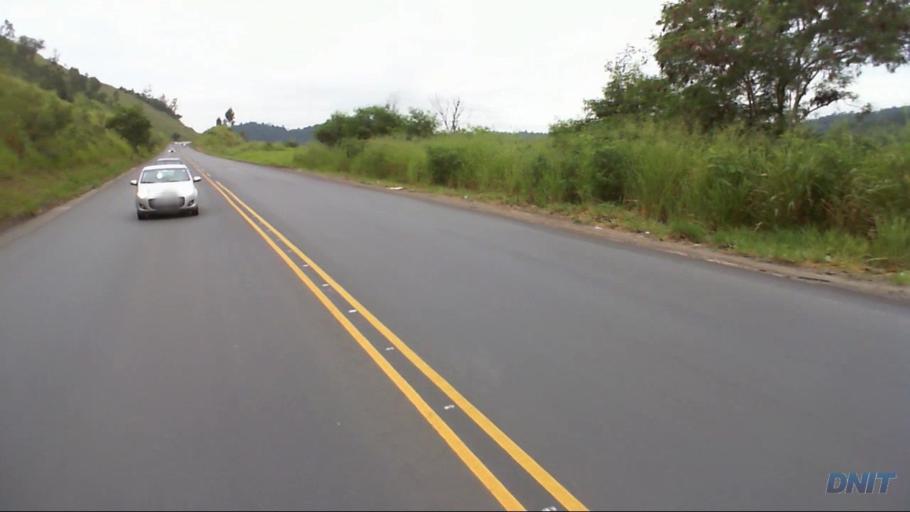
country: BR
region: Minas Gerais
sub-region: Coronel Fabriciano
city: Coronel Fabriciano
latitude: -19.5345
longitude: -42.5888
